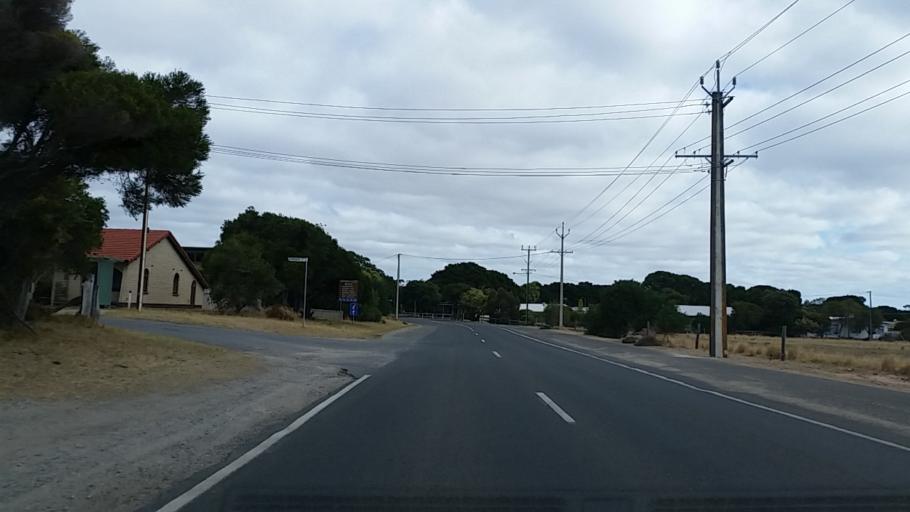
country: AU
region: South Australia
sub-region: Yankalilla
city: Normanville
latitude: -35.4433
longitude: 138.3166
